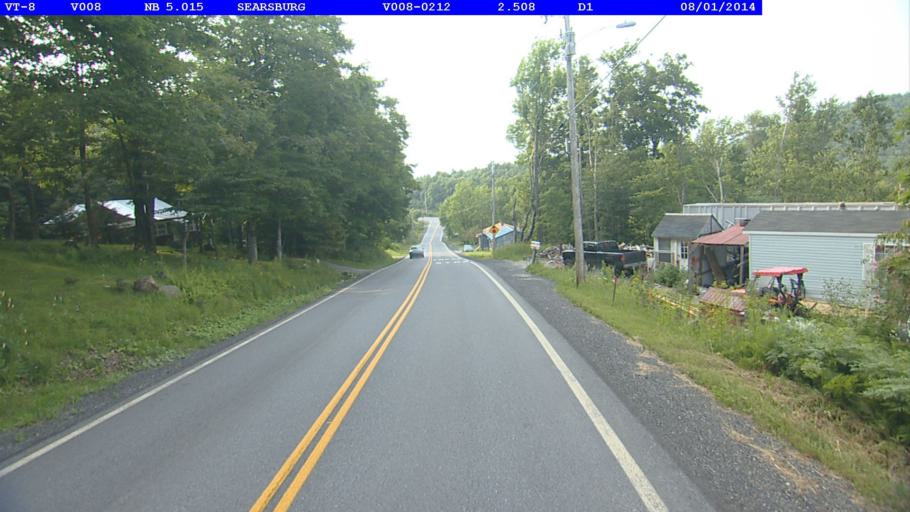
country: US
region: Vermont
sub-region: Windham County
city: Dover
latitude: 42.8925
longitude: -72.9749
